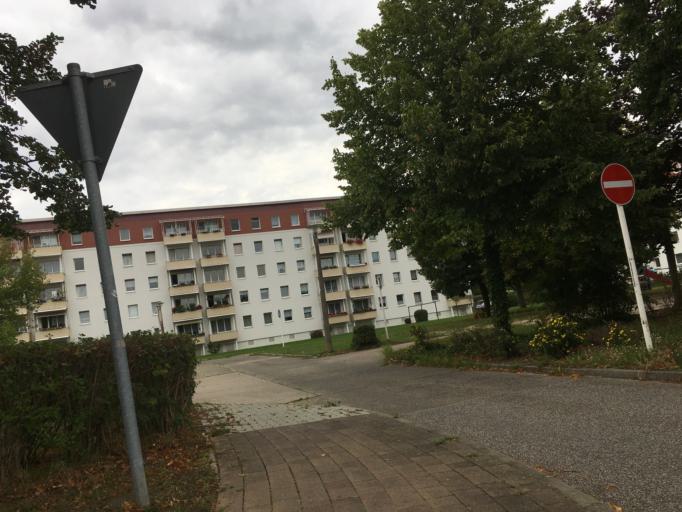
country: DE
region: Brandenburg
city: Schwedt (Oder)
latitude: 53.0633
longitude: 14.2786
